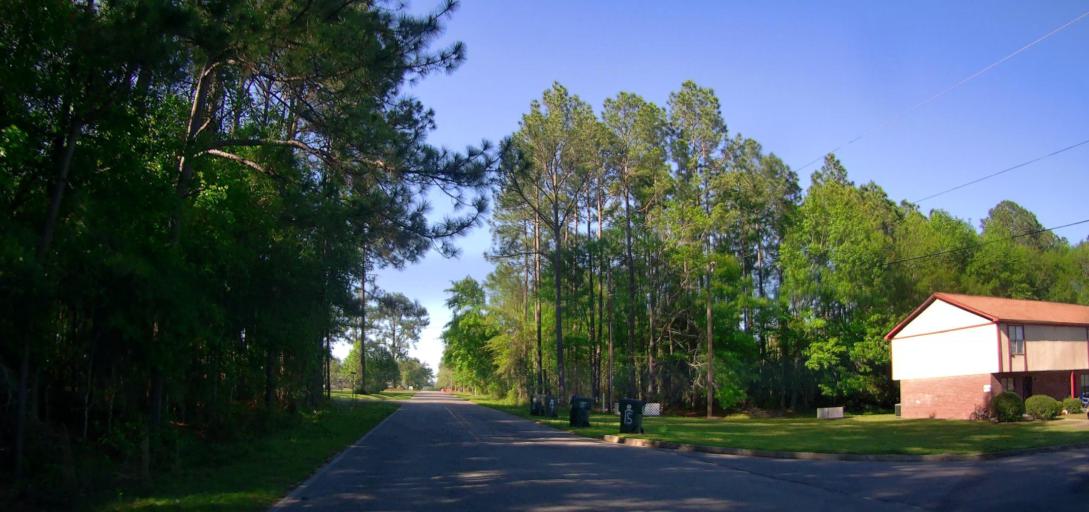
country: US
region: Georgia
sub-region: Wilcox County
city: Rochelle
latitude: 31.9446
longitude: -83.4483
